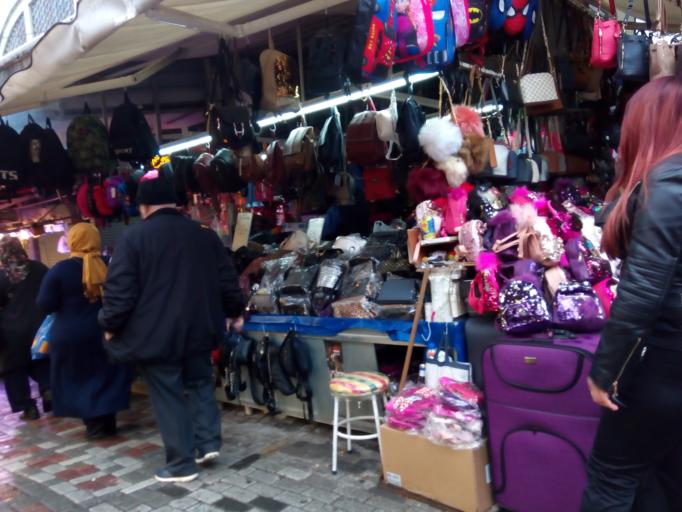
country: TR
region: Bursa
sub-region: Osmangazi
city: Bursa
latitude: 40.1846
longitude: 29.0649
